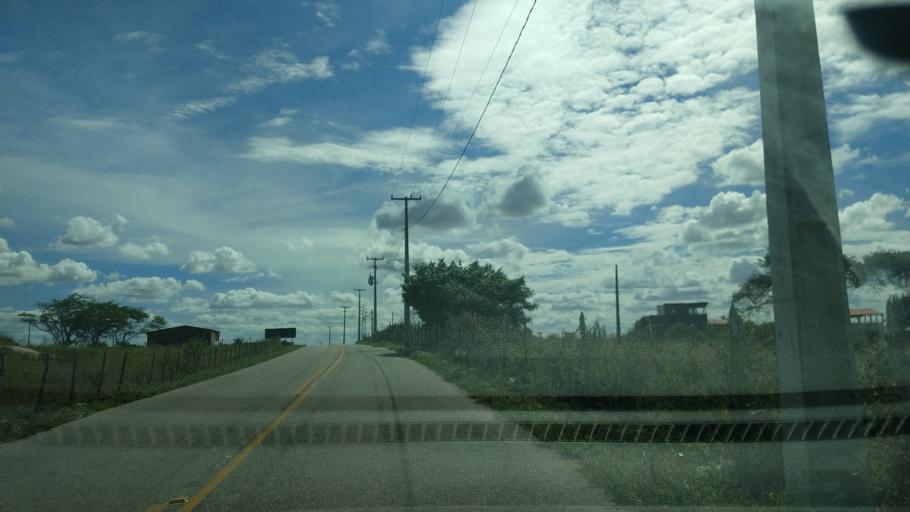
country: BR
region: Rio Grande do Norte
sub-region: Sao Jose Do Campestre
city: Sao Jose do Campestre
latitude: -6.4208
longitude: -35.7534
